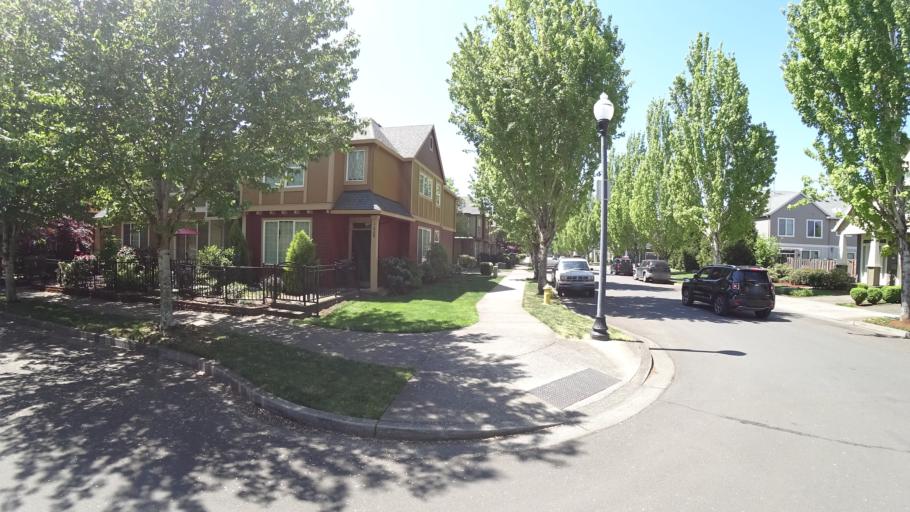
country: US
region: Oregon
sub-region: Washington County
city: Hillsboro
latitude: 45.5103
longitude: -122.9716
